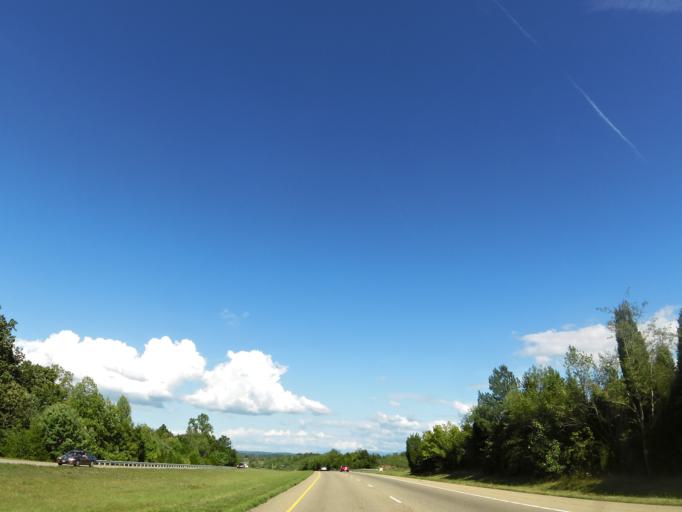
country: US
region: Tennessee
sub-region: Greene County
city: Mosheim
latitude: 36.1870
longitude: -82.9723
